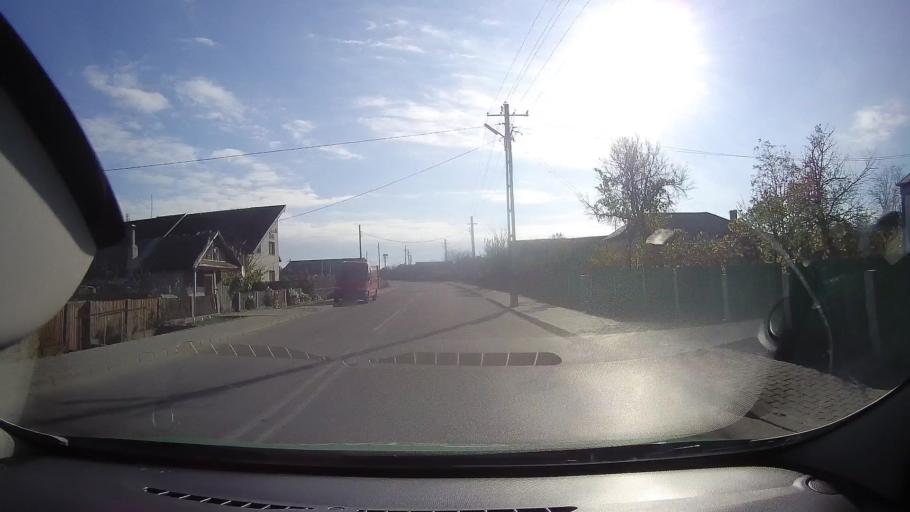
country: RO
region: Tulcea
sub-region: Comuna Murighiol
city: Murighiol
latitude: 45.0385
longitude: 29.1597
